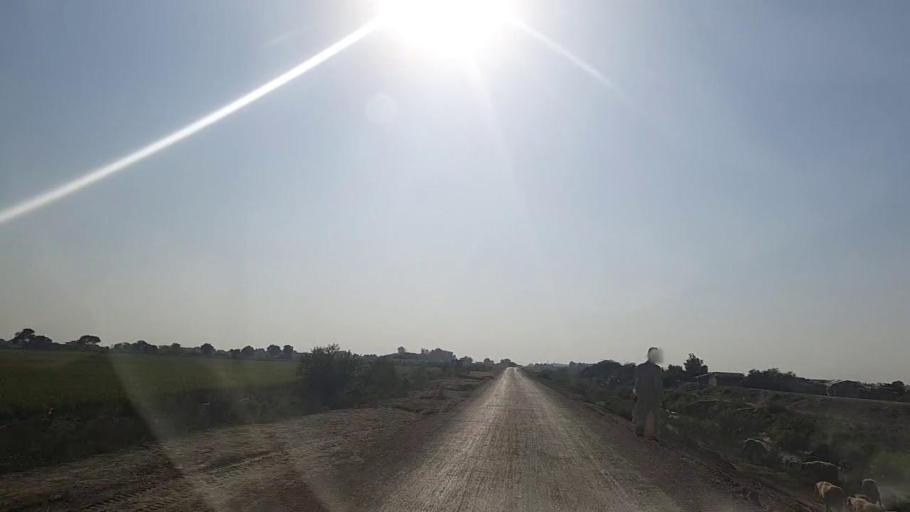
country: PK
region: Sindh
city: Mirpur Batoro
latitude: 24.5452
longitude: 68.1536
